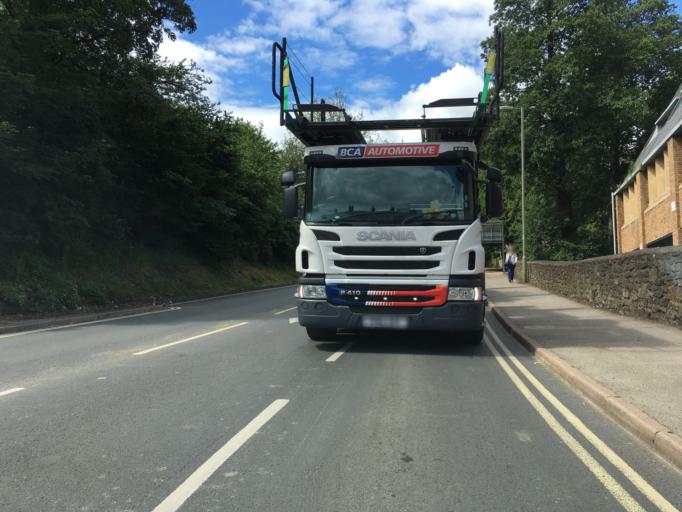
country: GB
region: England
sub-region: Oxfordshire
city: Banbury
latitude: 52.0573
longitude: -1.3406
